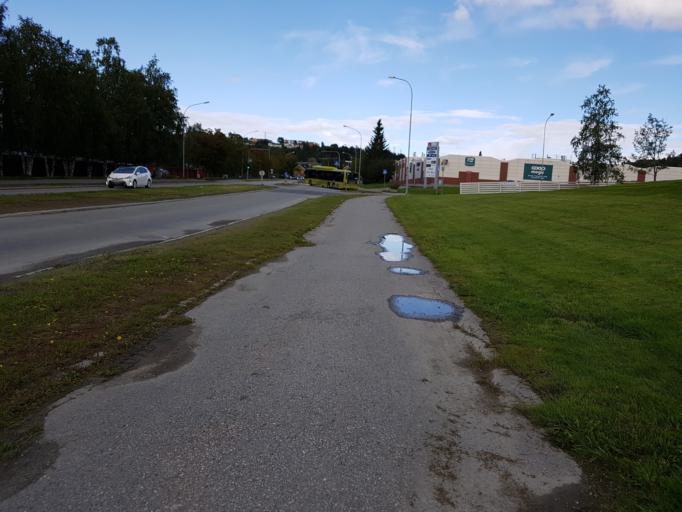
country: NO
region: Sor-Trondelag
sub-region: Trondheim
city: Trondheim
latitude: 63.4023
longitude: 10.4251
